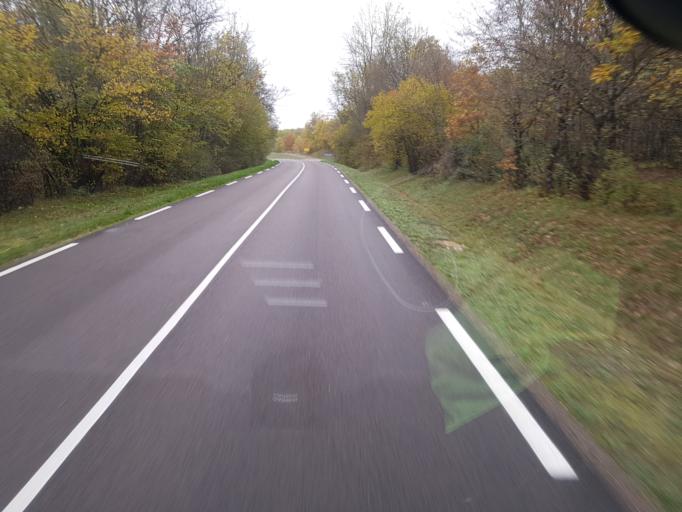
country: FR
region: Bourgogne
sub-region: Departement de la Cote-d'Or
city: Is-sur-Tille
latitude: 47.5226
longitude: 5.0013
